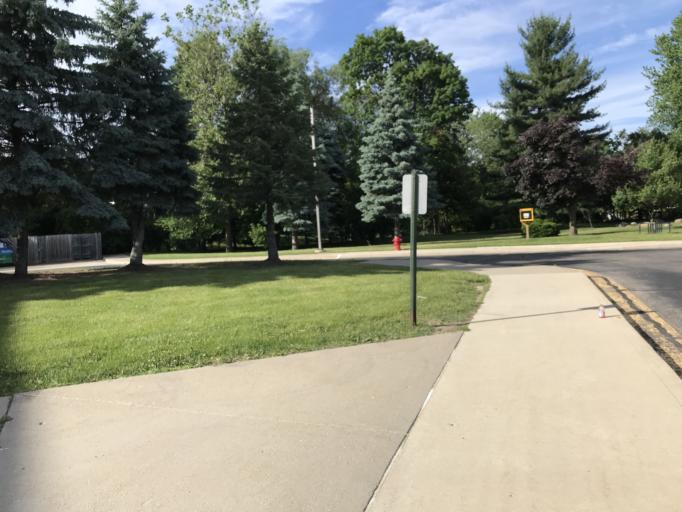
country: US
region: Michigan
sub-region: Oakland County
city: Farmington
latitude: 42.4632
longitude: -83.3919
